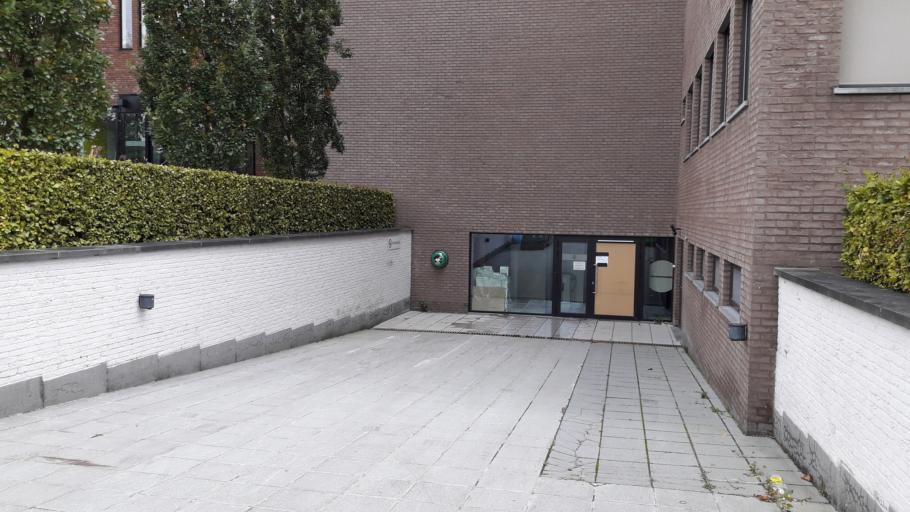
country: BE
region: Flanders
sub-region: Provincie West-Vlaanderen
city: Kortrijk
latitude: 50.8071
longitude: 3.2845
